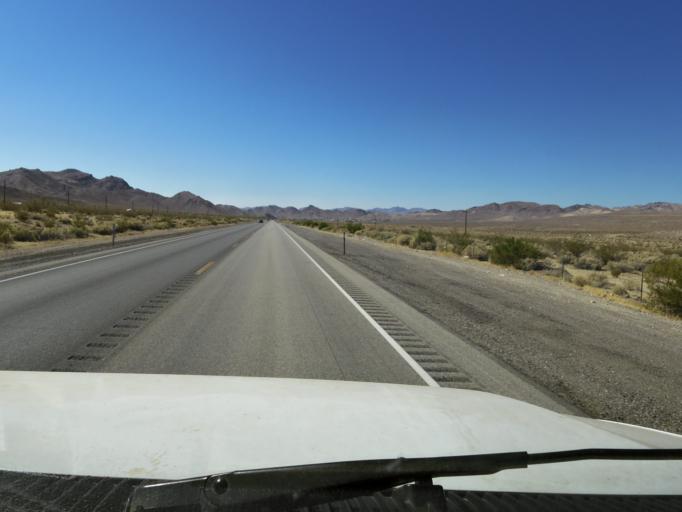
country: US
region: Nevada
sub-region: Nye County
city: Beatty
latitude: 36.9373
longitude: -116.7255
